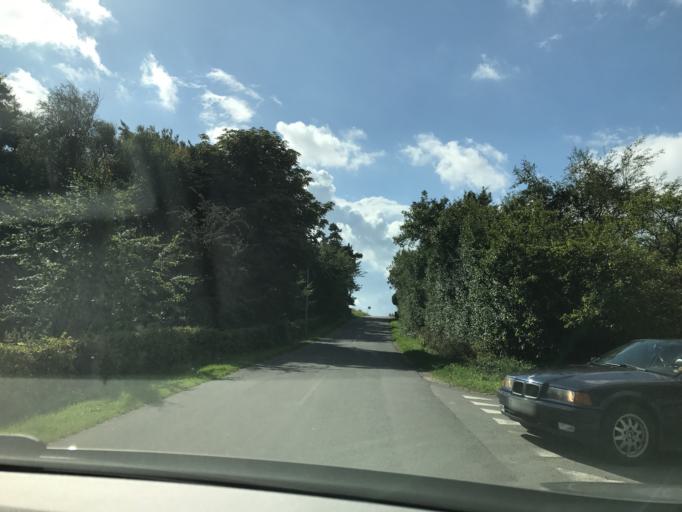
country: DK
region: South Denmark
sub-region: Middelfart Kommune
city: Norre Aby
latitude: 55.4590
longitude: 9.7981
